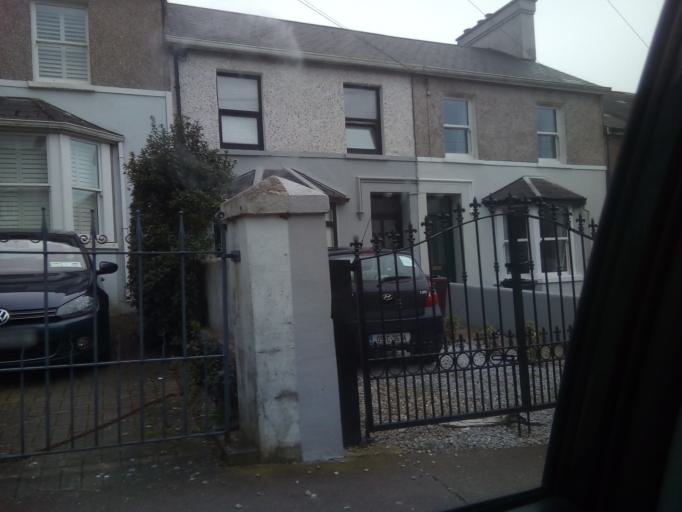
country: IE
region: Munster
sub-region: County Cork
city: Cork
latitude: 51.8910
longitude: -8.4938
